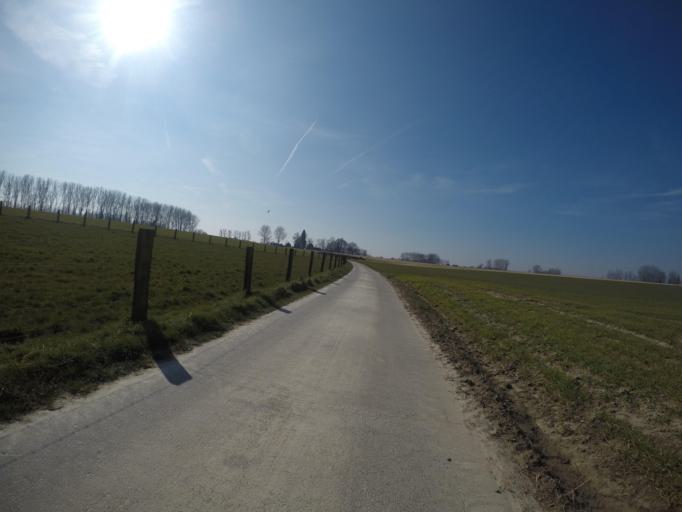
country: BE
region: Flanders
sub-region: Provincie Oost-Vlaanderen
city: Geraardsbergen
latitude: 50.7870
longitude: 3.8588
